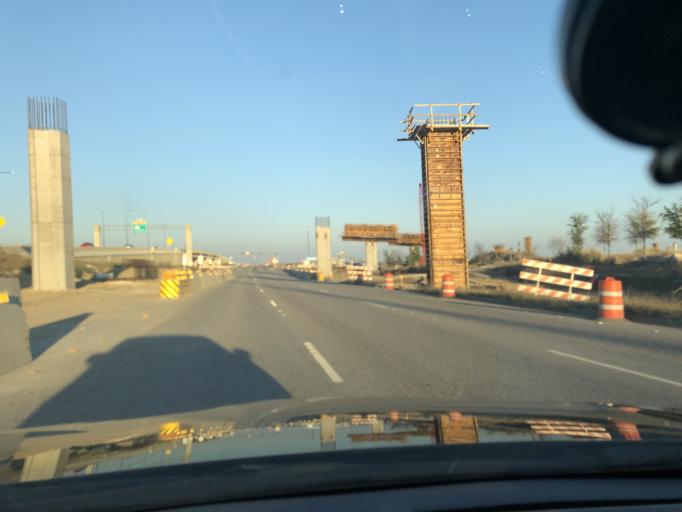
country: US
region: Texas
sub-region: Travis County
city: Manor
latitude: 30.3390
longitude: -97.5939
